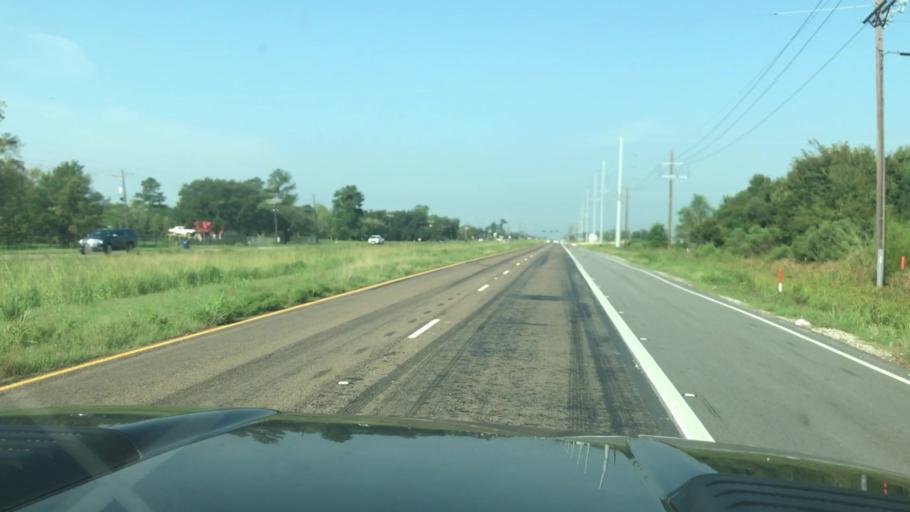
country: US
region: Texas
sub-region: Jefferson County
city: Bevil Oaks
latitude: 30.0631
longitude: -94.2230
